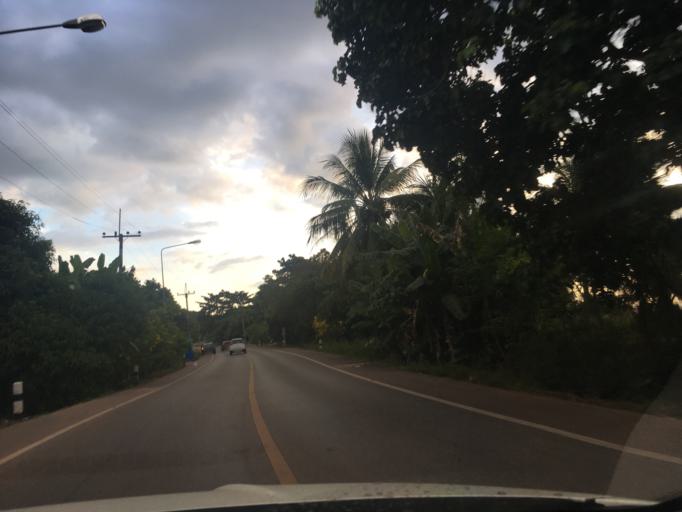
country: TH
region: Chanthaburi
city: Tha Mai
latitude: 12.6418
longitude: 101.8637
